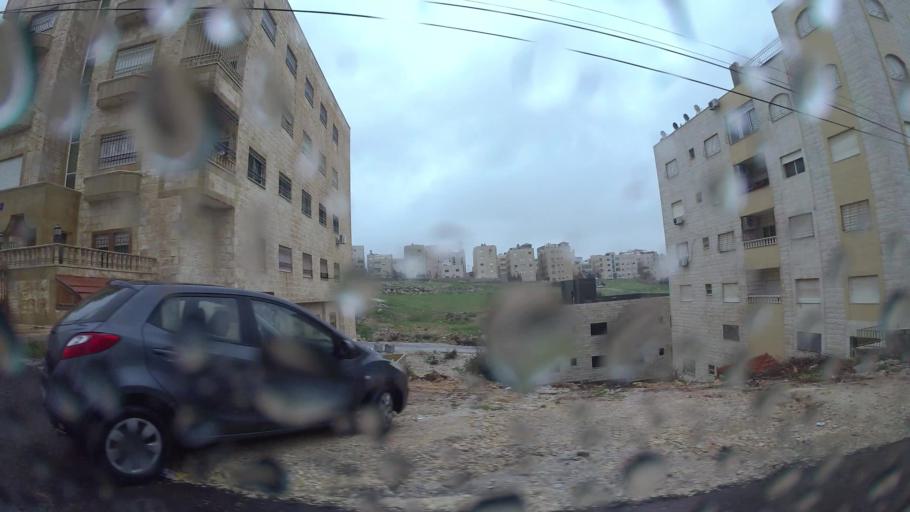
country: JO
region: Amman
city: Al Jubayhah
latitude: 32.0454
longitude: 35.8903
